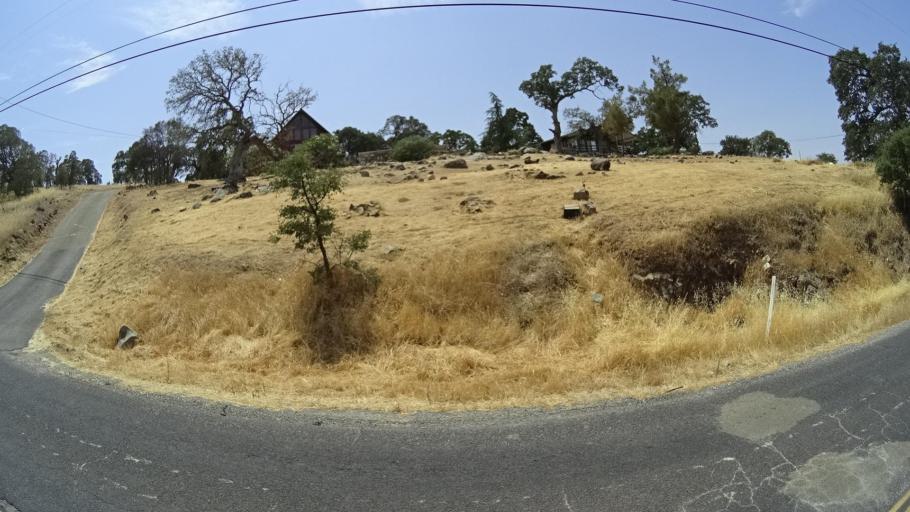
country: US
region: California
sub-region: Tuolumne County
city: Jamestown
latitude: 37.6695
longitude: -120.3566
